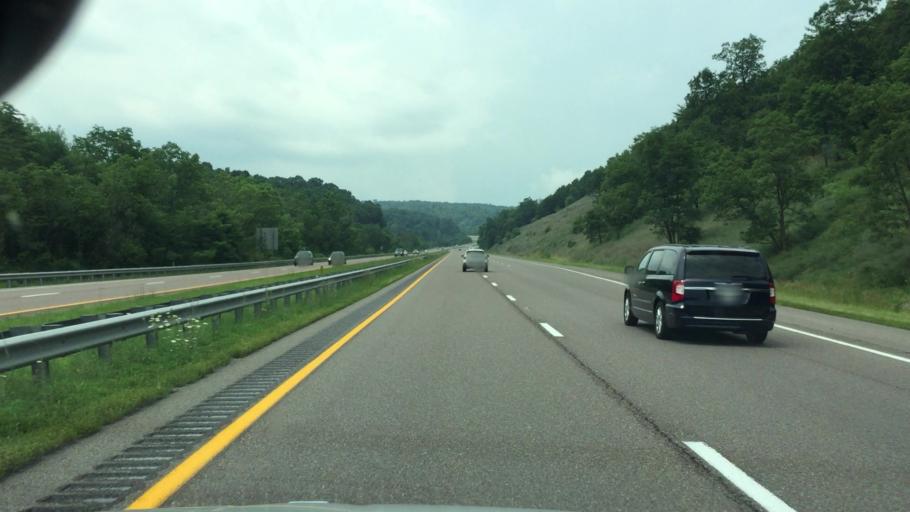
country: US
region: Maryland
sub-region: Allegany County
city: Cumberland
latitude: 39.6837
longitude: -78.4953
